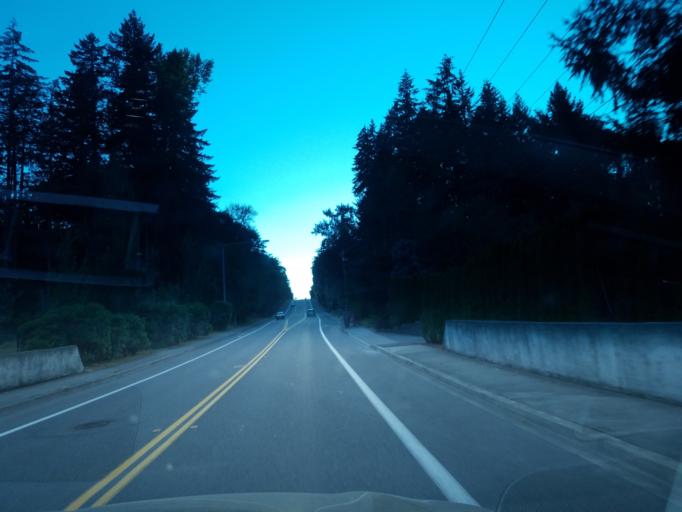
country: US
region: Washington
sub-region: King County
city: City of Sammamish
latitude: 47.6017
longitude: -122.0252
